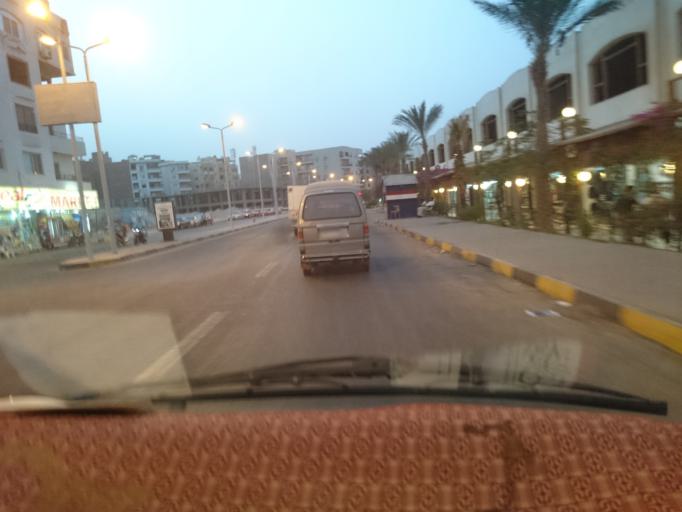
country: EG
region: Red Sea
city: Hurghada
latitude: 27.2396
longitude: 33.8448
